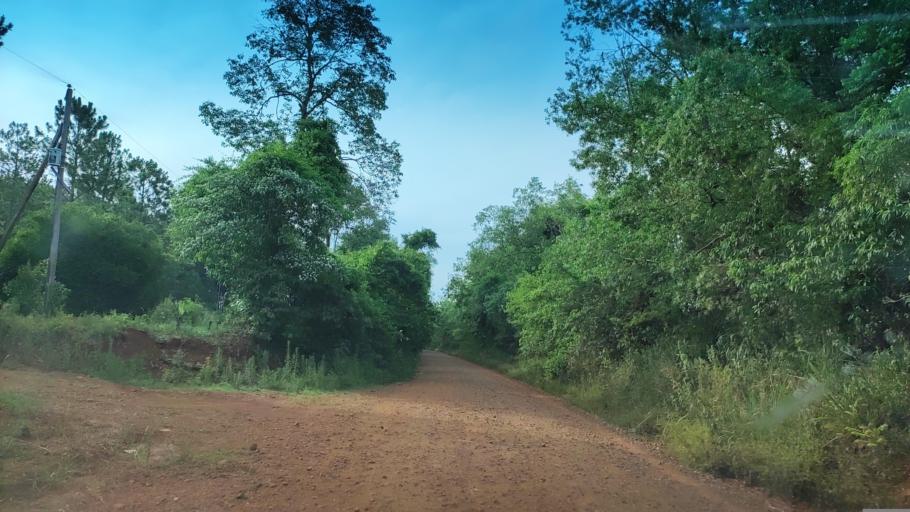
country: AR
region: Misiones
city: Gobernador Roca
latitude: -27.1710
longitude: -55.5080
